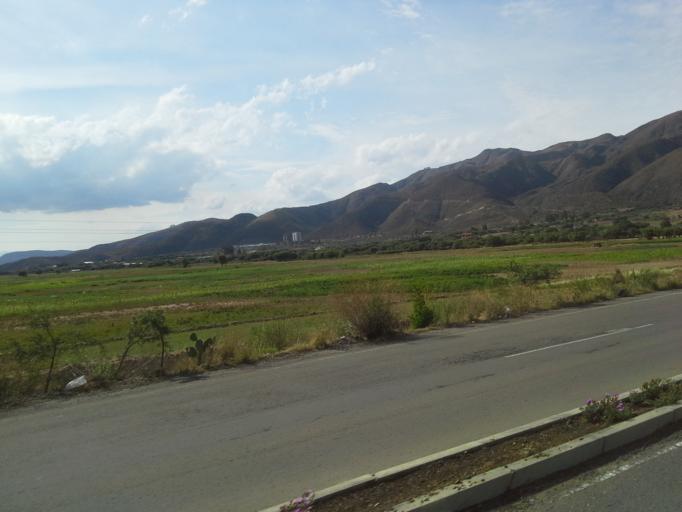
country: BO
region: Cochabamba
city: Tarata
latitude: -17.5506
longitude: -66.0069
